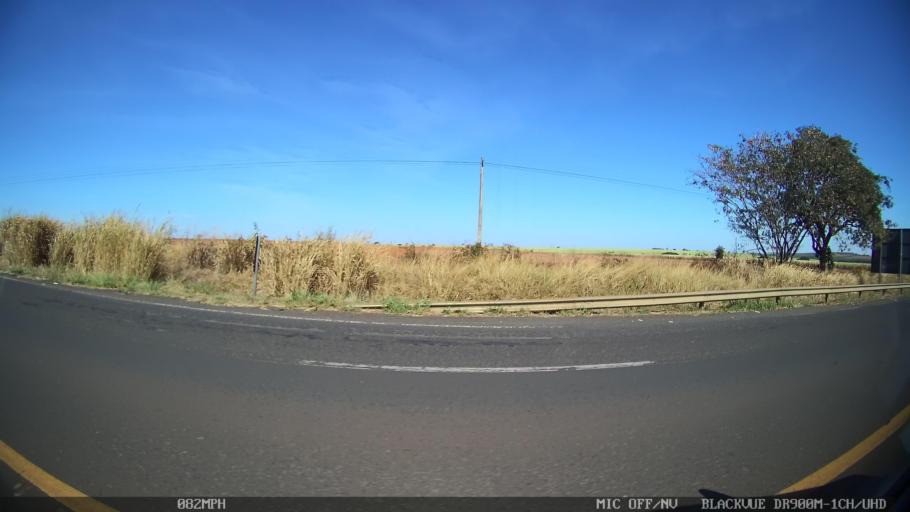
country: BR
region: Sao Paulo
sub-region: Barretos
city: Barretos
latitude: -20.5575
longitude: -48.6462
